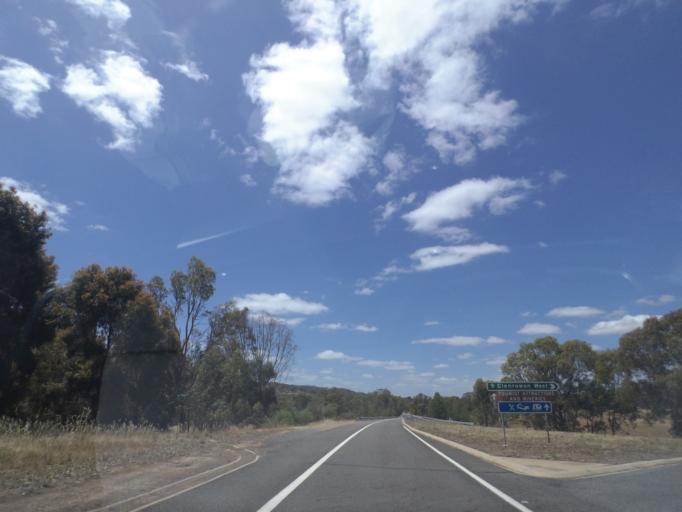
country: AU
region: Victoria
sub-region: Wangaratta
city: Wangaratta
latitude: -36.4666
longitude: 146.2108
